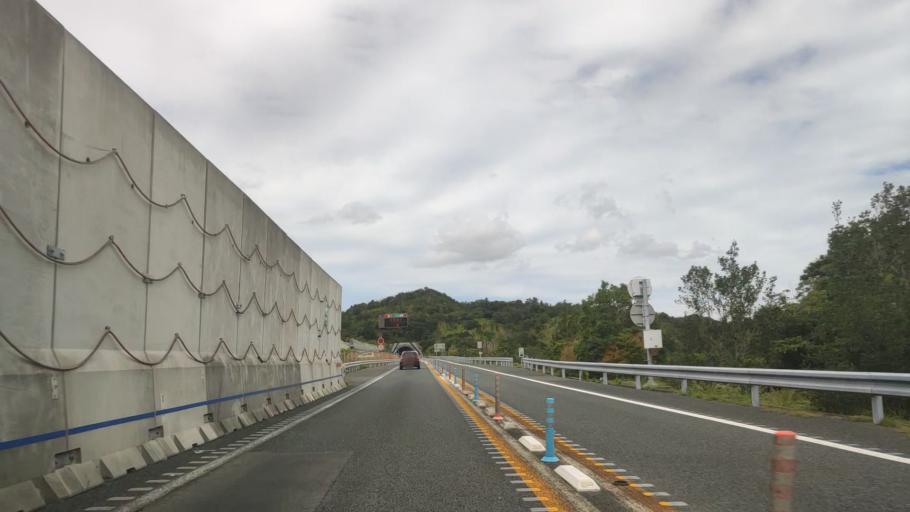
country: JP
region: Wakayama
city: Gobo
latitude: 33.8731
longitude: 135.1882
